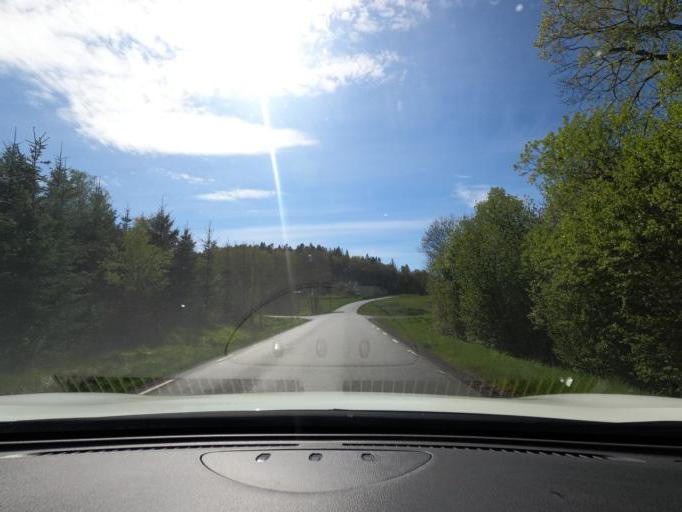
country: SE
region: Vaestra Goetaland
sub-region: Marks Kommun
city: Kinna
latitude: 57.4750
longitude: 12.5826
